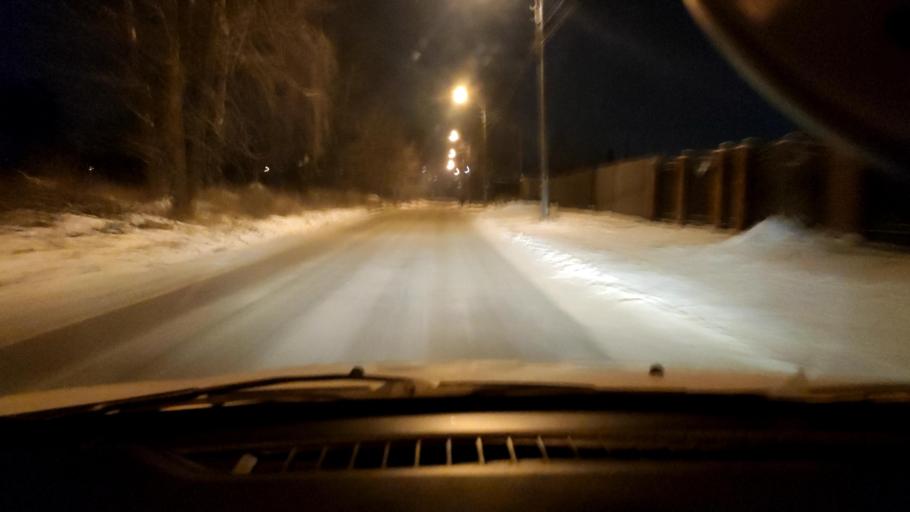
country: RU
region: Perm
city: Overyata
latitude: 58.0103
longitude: 55.9452
